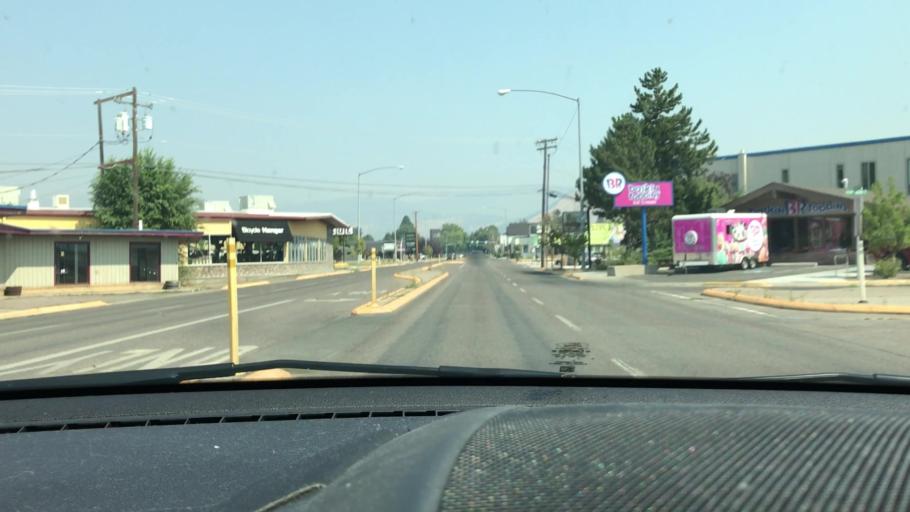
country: US
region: Montana
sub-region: Missoula County
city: Missoula
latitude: 46.8533
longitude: -114.0112
